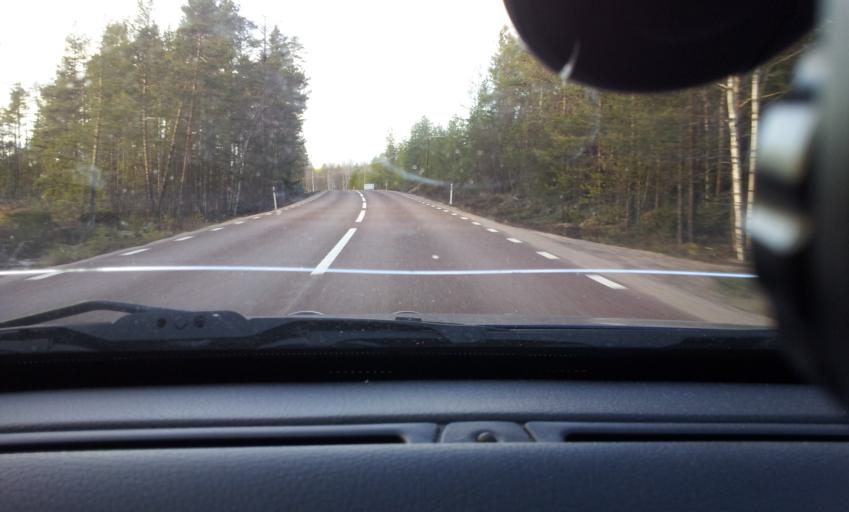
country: SE
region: Jaemtland
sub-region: Harjedalens Kommun
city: Sveg
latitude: 62.1357
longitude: 14.9697
